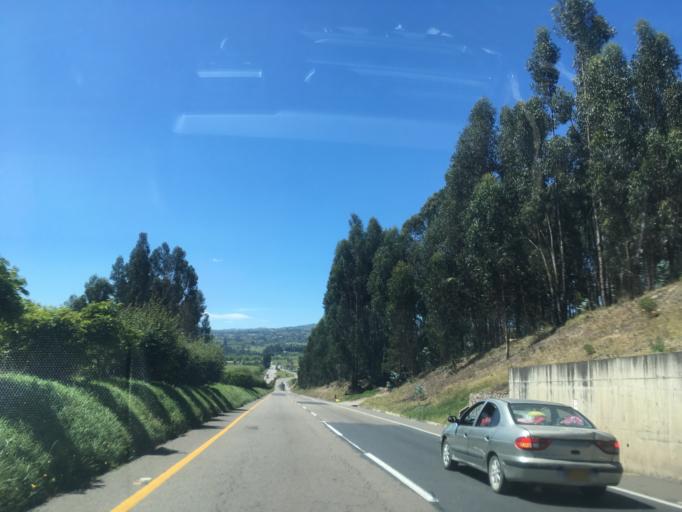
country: CO
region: Boyaca
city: Tuta
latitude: 5.7141
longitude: -73.2321
